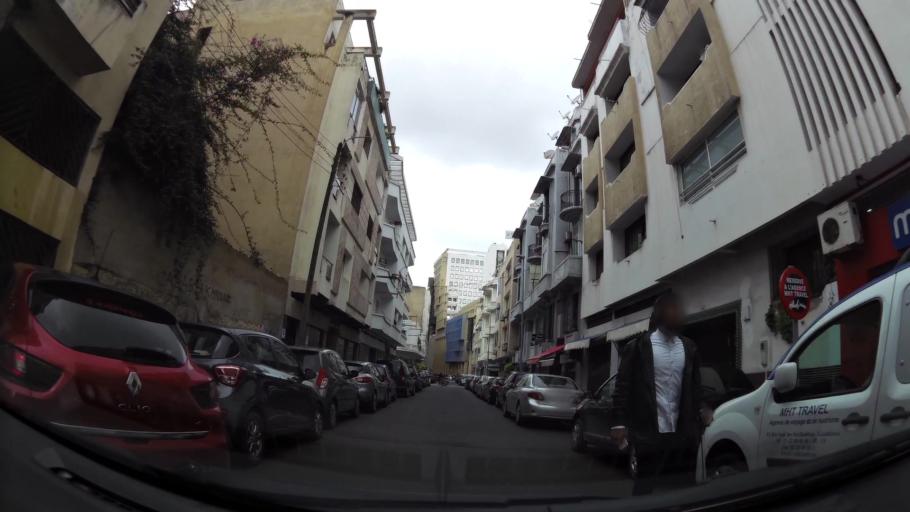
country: MA
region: Grand Casablanca
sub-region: Casablanca
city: Casablanca
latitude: 33.5842
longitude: -7.6208
